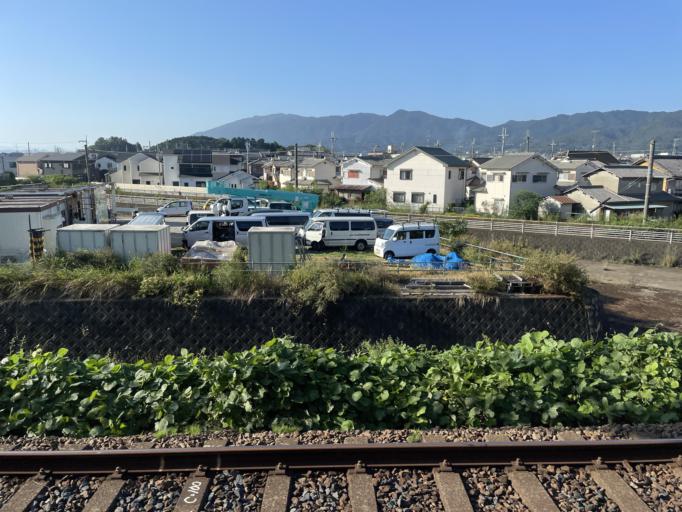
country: JP
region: Nara
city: Tawaramoto
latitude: 34.5401
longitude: 135.7092
